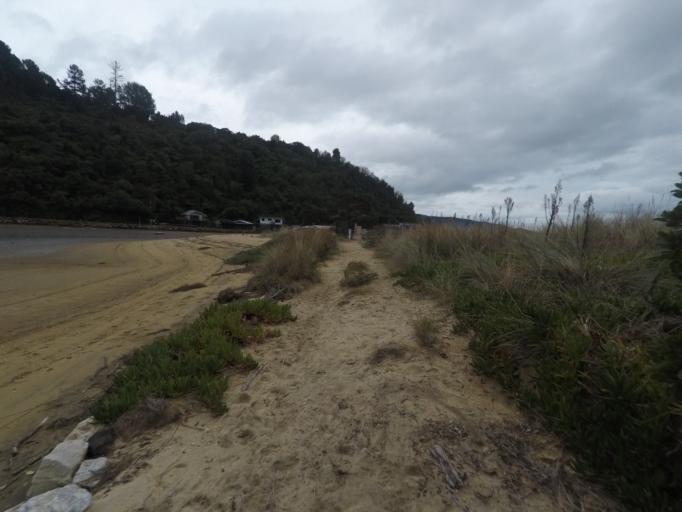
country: NZ
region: Tasman
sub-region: Tasman District
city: Motueka
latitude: -41.0102
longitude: 173.0073
